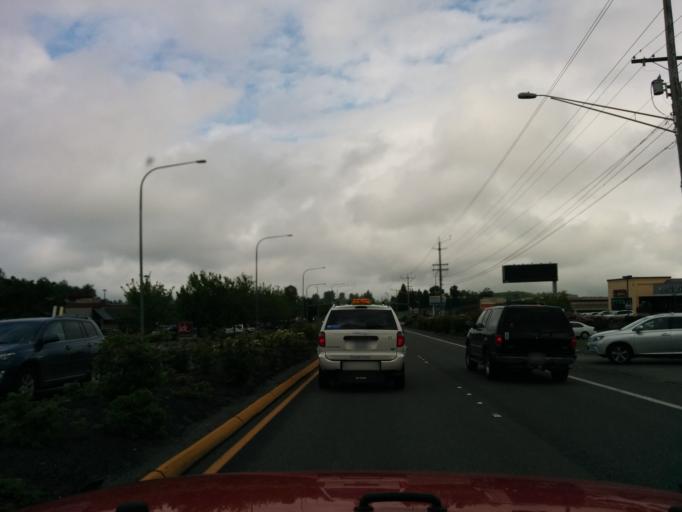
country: US
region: Washington
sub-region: Snohomish County
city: Mukilteo
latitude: 47.8907
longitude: -122.2855
